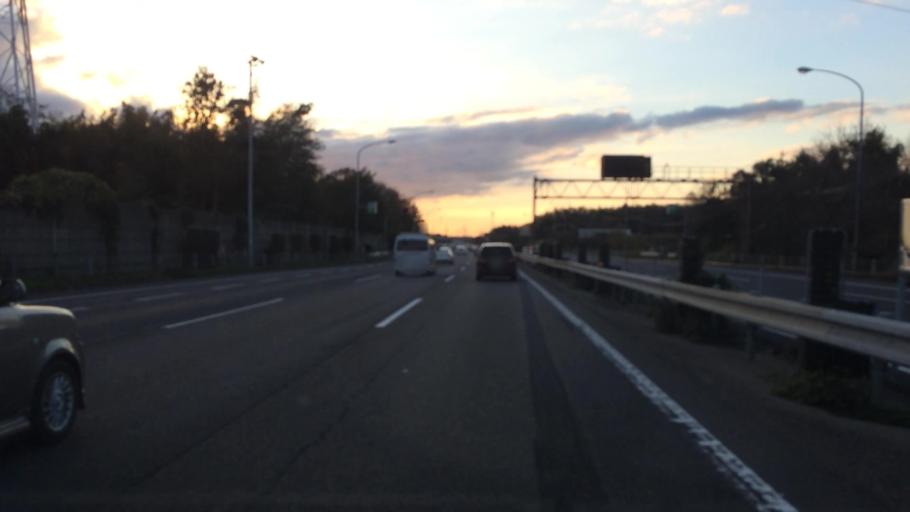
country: JP
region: Chiba
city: Yotsukaido
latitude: 35.6842
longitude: 140.1735
